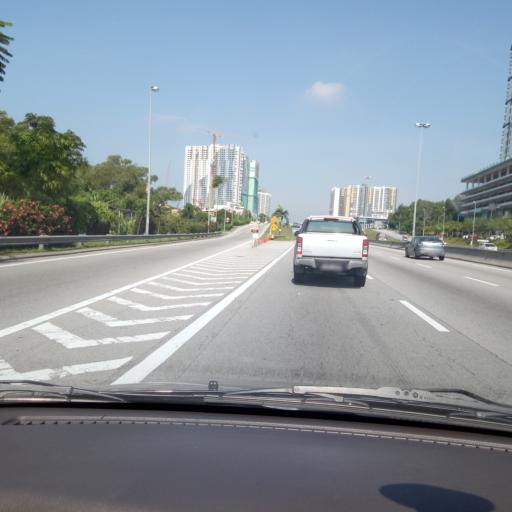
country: MY
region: Selangor
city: Kampong Baharu Balakong
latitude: 3.0294
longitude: 101.7596
